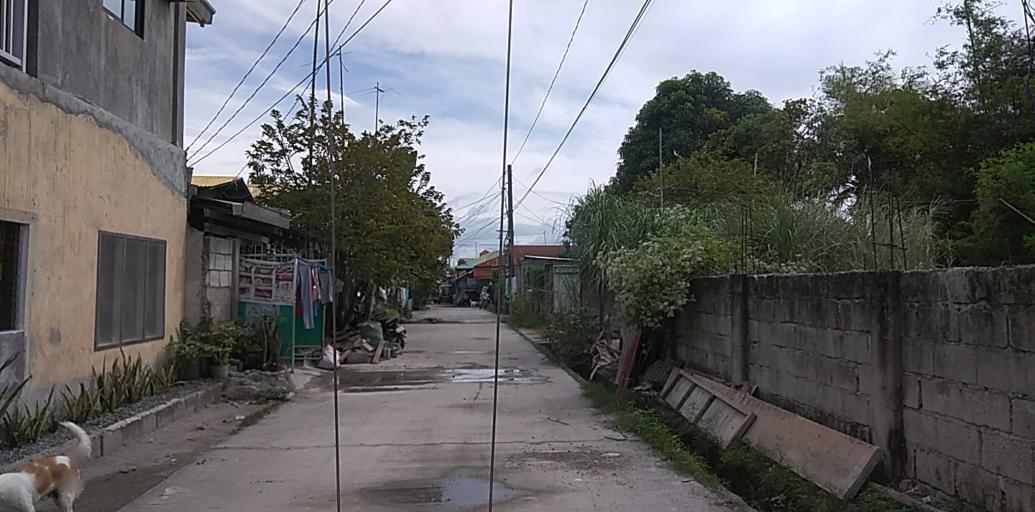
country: PH
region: Central Luzon
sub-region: Province of Pampanga
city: Manibaug Pasig
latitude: 15.1070
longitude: 120.5595
